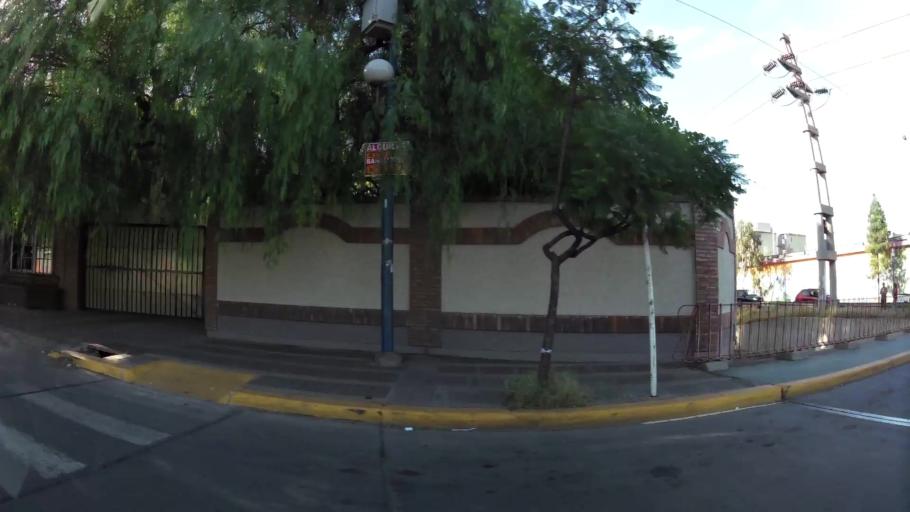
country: AR
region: Mendoza
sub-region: Departamento de Godoy Cruz
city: Godoy Cruz
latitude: -32.9128
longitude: -68.8385
